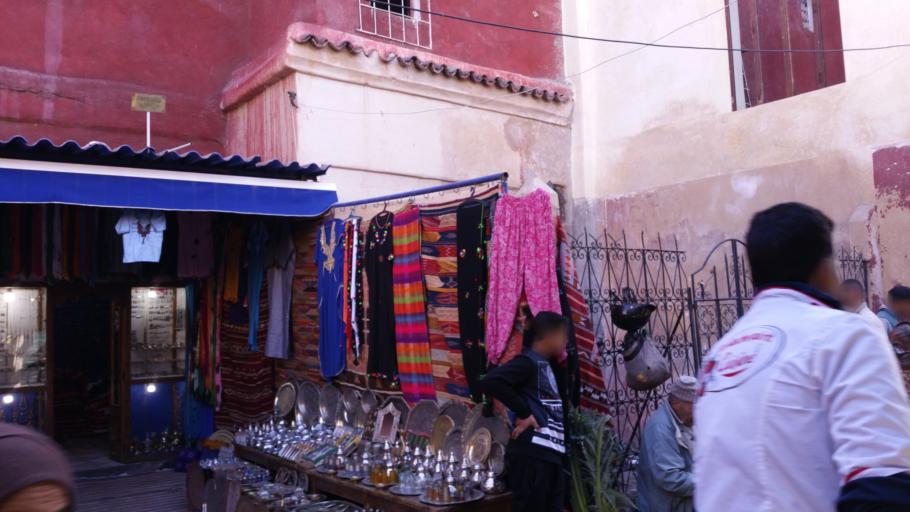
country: MA
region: Marrakech-Tensift-Al Haouz
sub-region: Marrakech
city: Marrakesh
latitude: 31.6236
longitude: -7.9848
